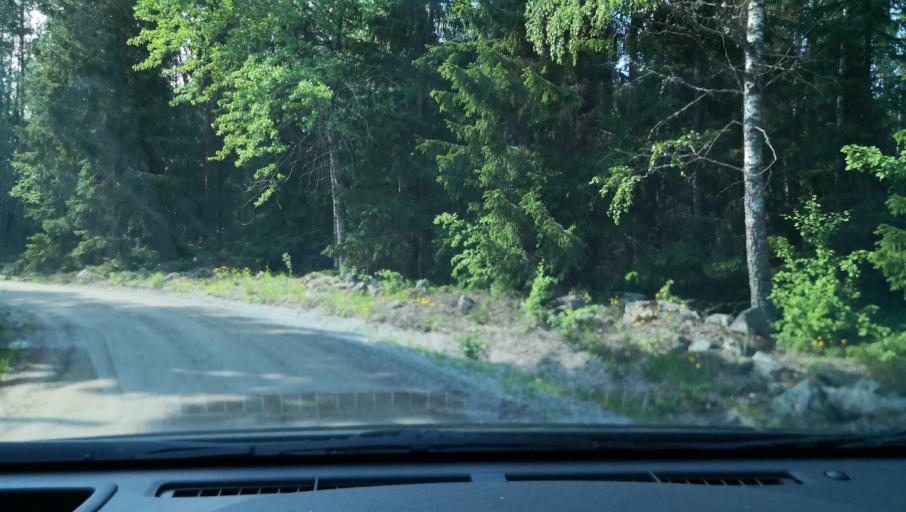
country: SE
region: Uppsala
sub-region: Enkopings Kommun
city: Orsundsbro
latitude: 59.8384
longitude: 17.2169
